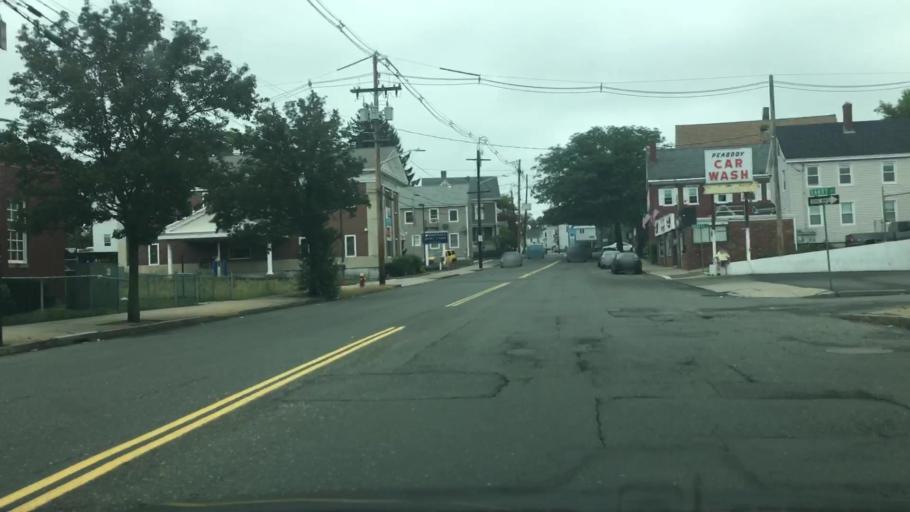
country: US
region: Massachusetts
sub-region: Essex County
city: Peabody
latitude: 42.5278
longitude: -70.9273
